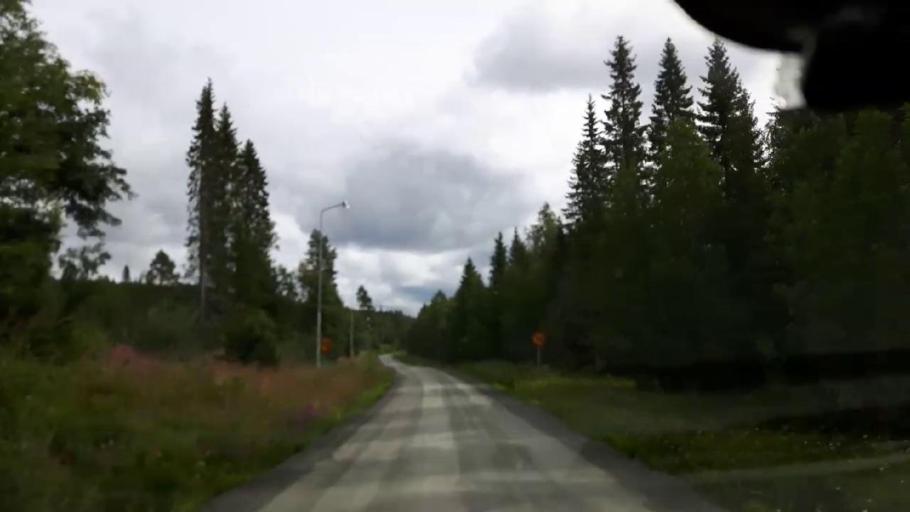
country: SE
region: Jaemtland
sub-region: Krokoms Kommun
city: Valla
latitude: 63.6250
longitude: 14.0440
